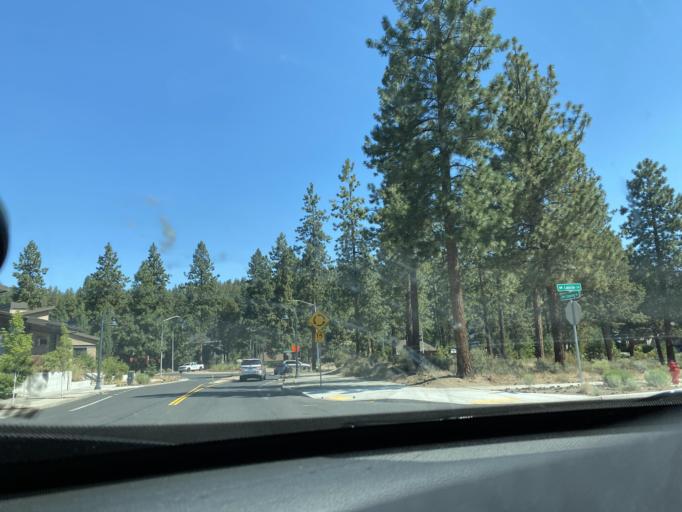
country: US
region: Oregon
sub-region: Deschutes County
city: Bend
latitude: 44.0632
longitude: -121.3453
